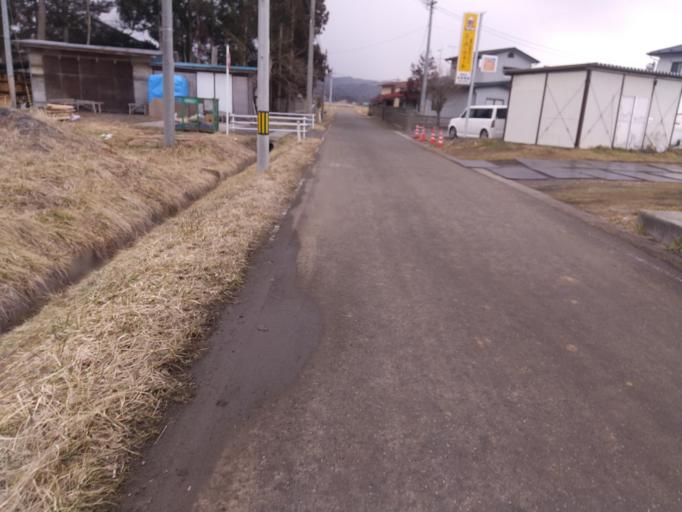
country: JP
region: Miyagi
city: Wakuya
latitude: 38.7005
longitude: 141.2658
